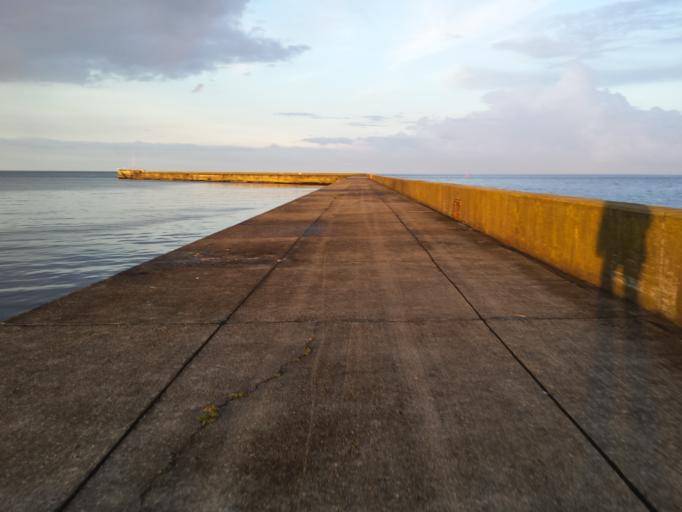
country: DE
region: Schleswig-Holstein
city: Helgoland
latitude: 54.1699
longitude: 7.8917
